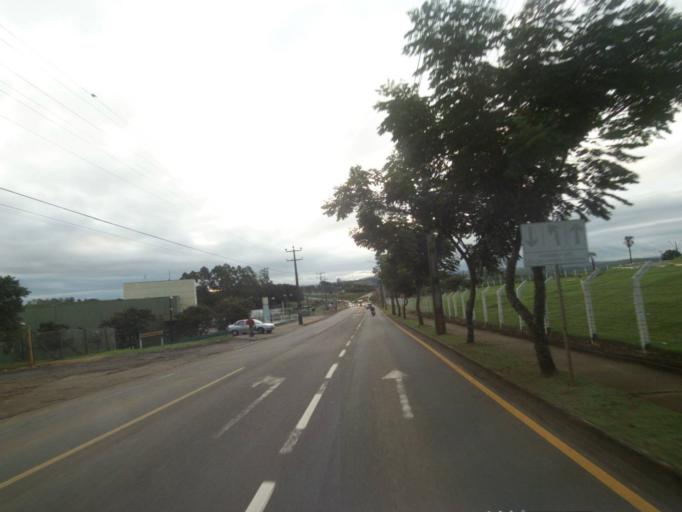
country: BR
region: Parana
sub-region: Telemaco Borba
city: Telemaco Borba
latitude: -24.3341
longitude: -50.6491
